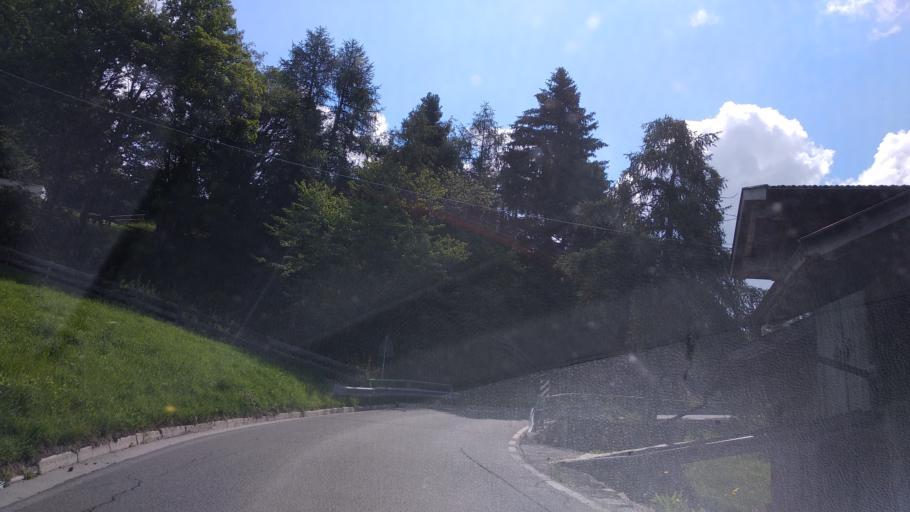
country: IT
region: Trentino-Alto Adige
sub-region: Bolzano
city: Avelengo
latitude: 46.6503
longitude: 11.2182
